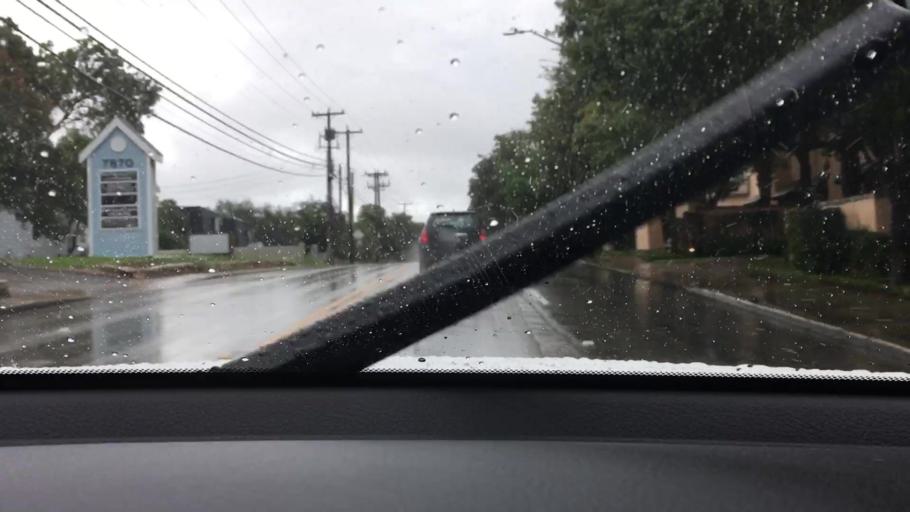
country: US
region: Texas
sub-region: Bexar County
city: Alamo Heights
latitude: 29.5052
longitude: -98.4663
